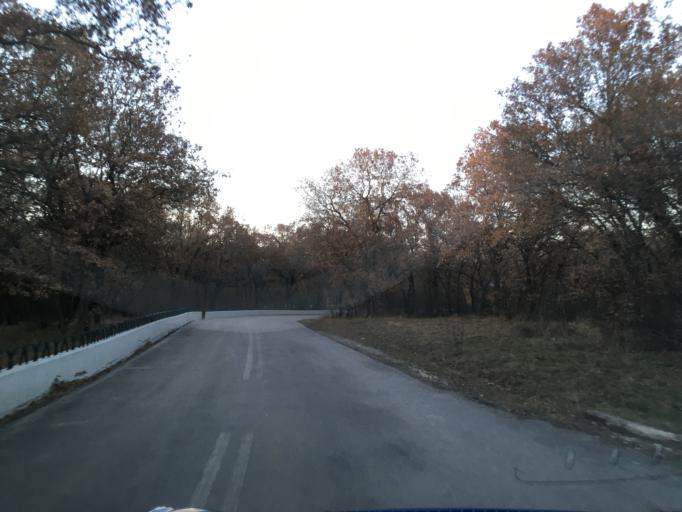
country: GR
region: West Macedonia
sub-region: Nomos Kozanis
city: Koila
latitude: 40.3291
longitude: 21.8320
